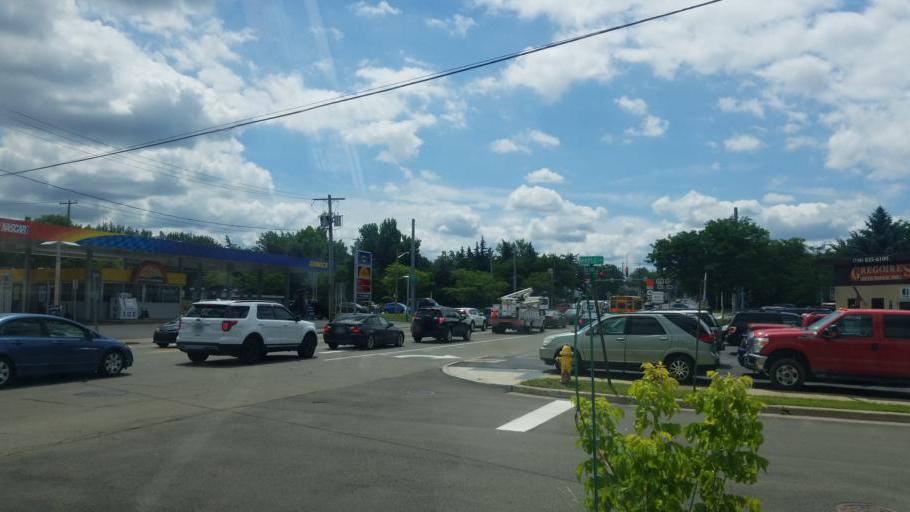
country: US
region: New York
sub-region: Erie County
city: Blasdell
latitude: 42.7901
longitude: -78.8241
